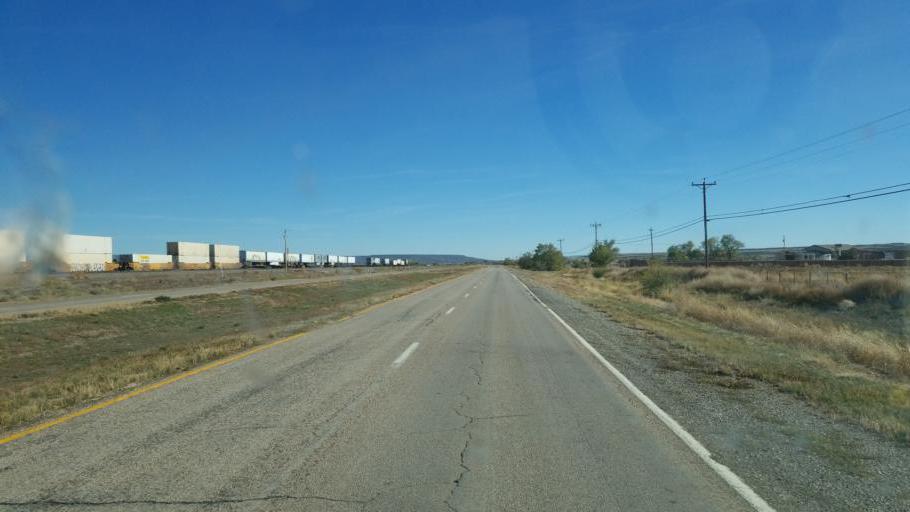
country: US
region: New Mexico
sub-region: Cibola County
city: Milan
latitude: 35.2587
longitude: -107.9664
